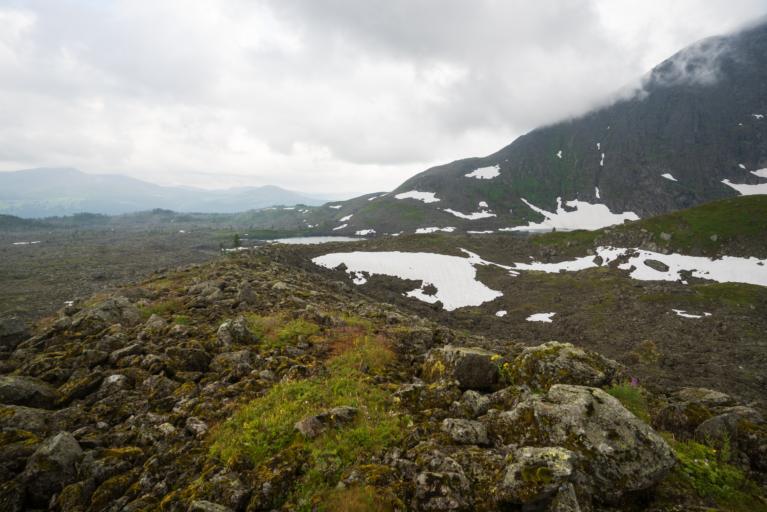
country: RU
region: Komi Republic
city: Synya
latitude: 64.7869
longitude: 58.9138
